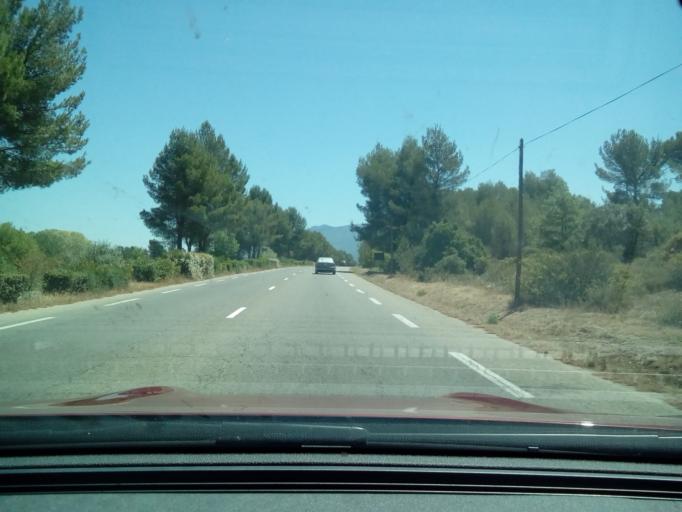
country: FR
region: Provence-Alpes-Cote d'Azur
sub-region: Departement des Bouches-du-Rhone
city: Peynier
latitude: 43.4609
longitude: 5.6353
